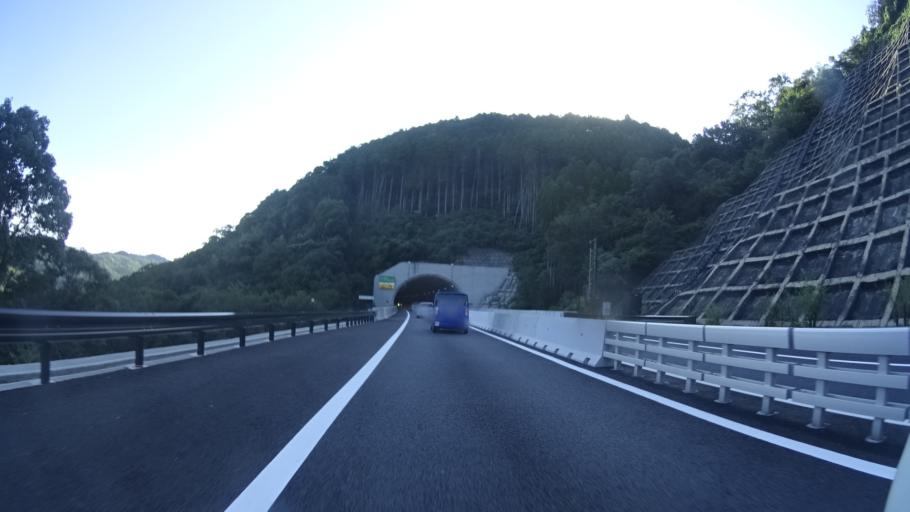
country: JP
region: Kumamoto
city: Ozu
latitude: 32.7474
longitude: 130.8452
